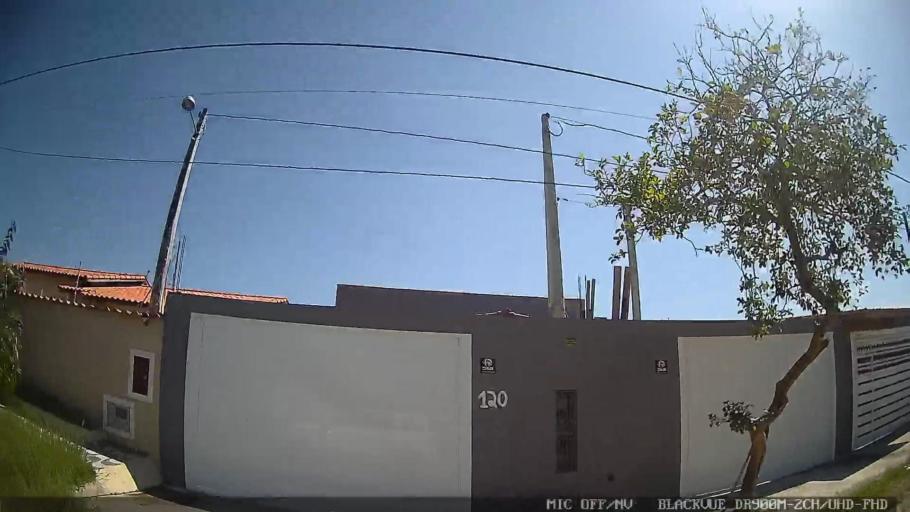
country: BR
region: Sao Paulo
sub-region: Itanhaem
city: Itanhaem
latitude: -24.2103
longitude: -46.8578
